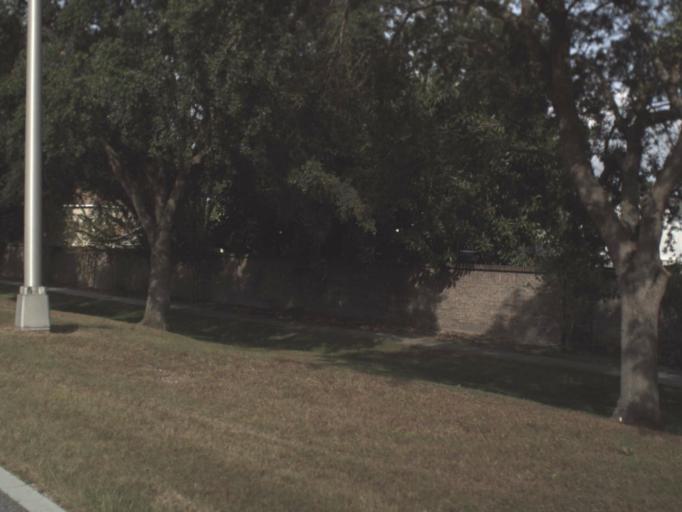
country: US
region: Florida
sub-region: Orange County
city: Hunters Creek
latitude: 28.3545
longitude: -81.4195
